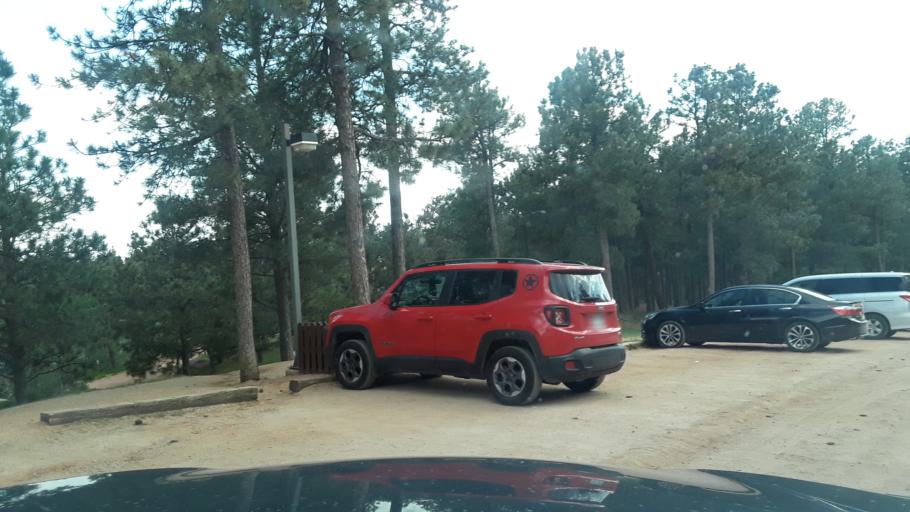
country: US
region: Colorado
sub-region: El Paso County
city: Gleneagle
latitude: 39.0610
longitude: -104.7918
